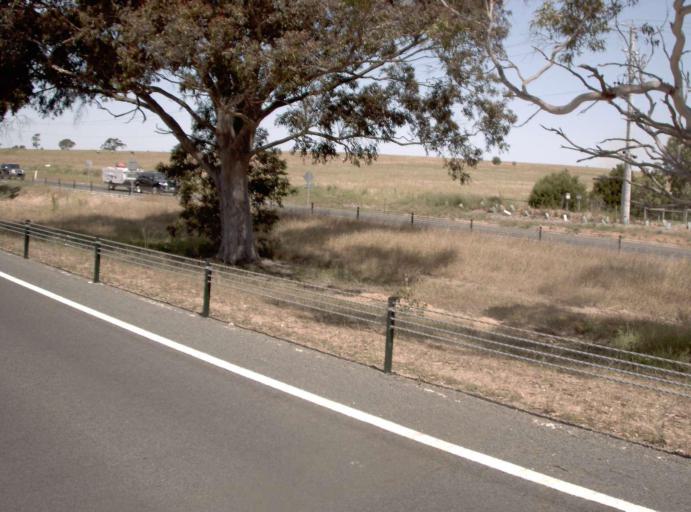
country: AU
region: Victoria
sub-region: Wellington
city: Sale
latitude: -38.1041
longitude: 147.0268
